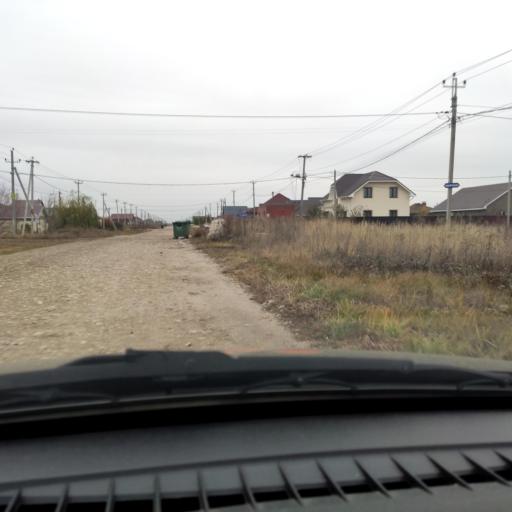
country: RU
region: Samara
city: Podstepki
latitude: 53.5251
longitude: 49.1543
